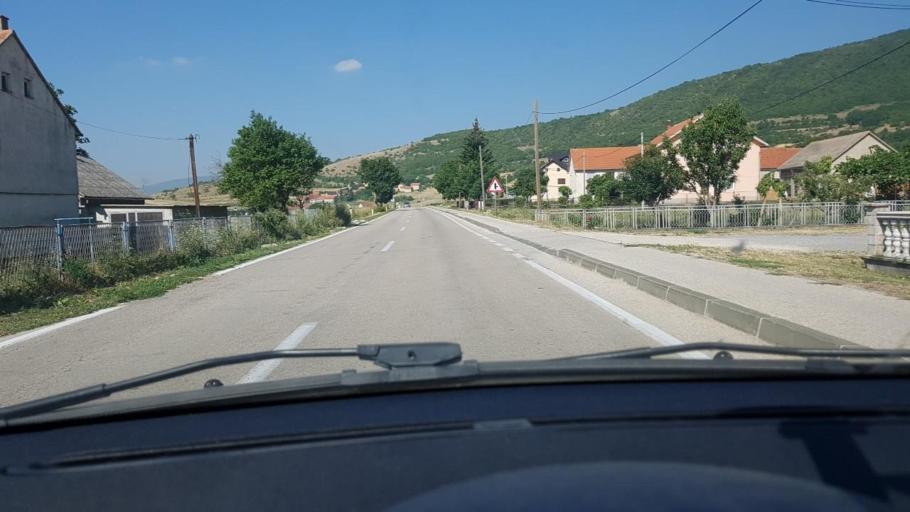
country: BA
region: Federation of Bosnia and Herzegovina
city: Zabrisce
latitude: 43.8697
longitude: 16.9175
